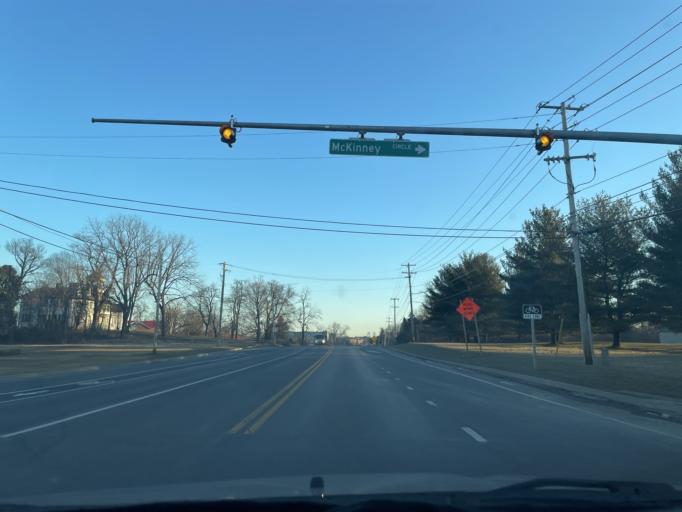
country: US
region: Maryland
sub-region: Frederick County
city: Ballenger Creek
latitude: 39.3617
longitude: -77.4185
